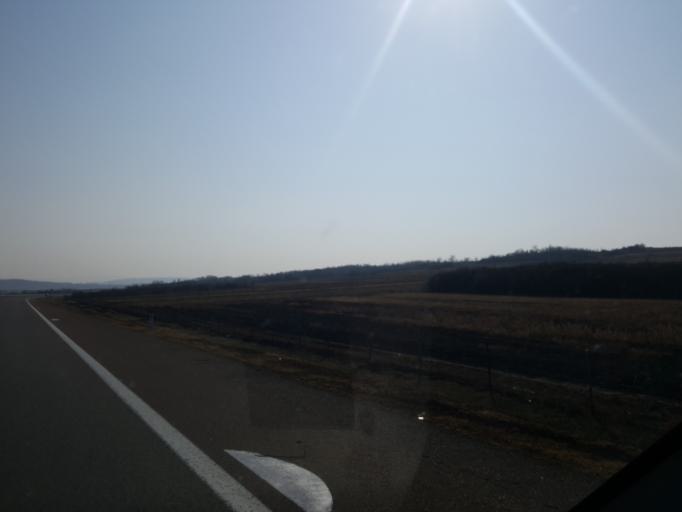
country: RS
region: Central Serbia
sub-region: Nisavski Okrug
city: Doljevac
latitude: 43.2528
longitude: 21.8151
